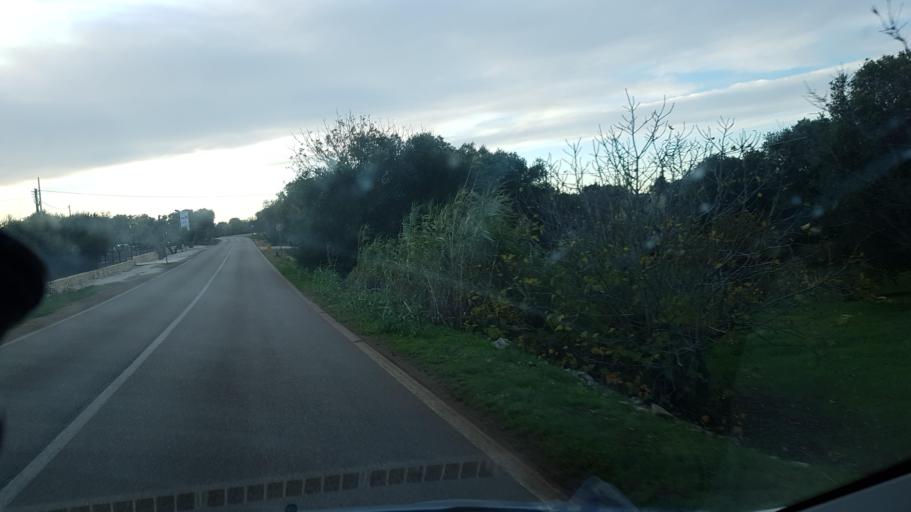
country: IT
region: Apulia
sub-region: Provincia di Brindisi
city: San Michele Salentino
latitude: 40.6450
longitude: 17.6393
